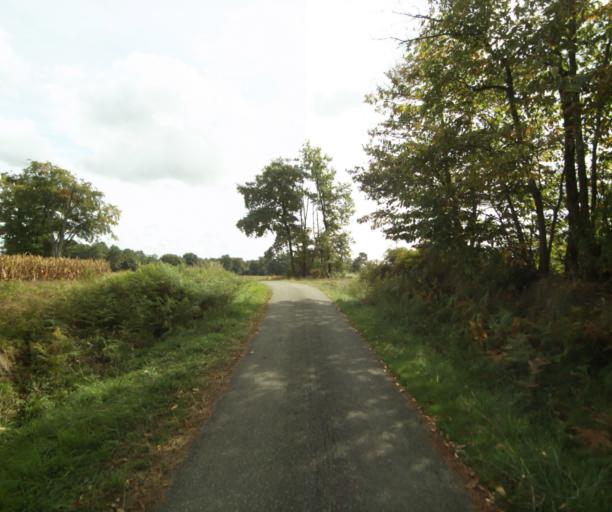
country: FR
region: Midi-Pyrenees
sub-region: Departement du Gers
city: Eauze
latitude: 43.8269
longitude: 0.0989
